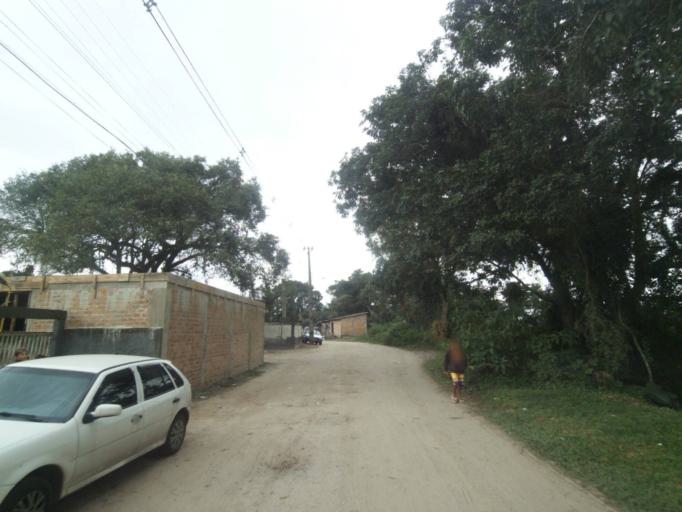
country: BR
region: Parana
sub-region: Paranagua
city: Paranagua
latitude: -25.5378
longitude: -48.5501
